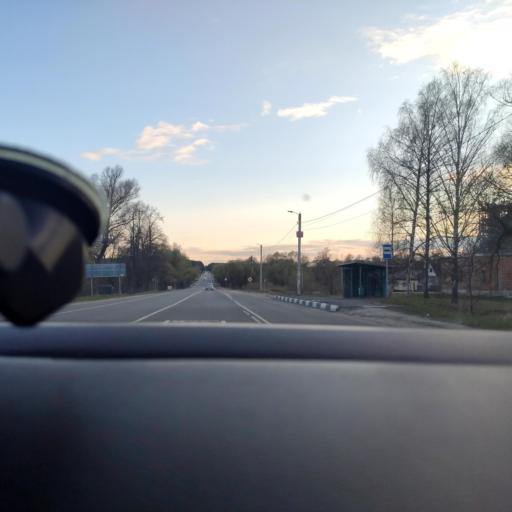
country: RU
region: Moskovskaya
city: Krasnyy Tkach
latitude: 55.4264
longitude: 39.1928
